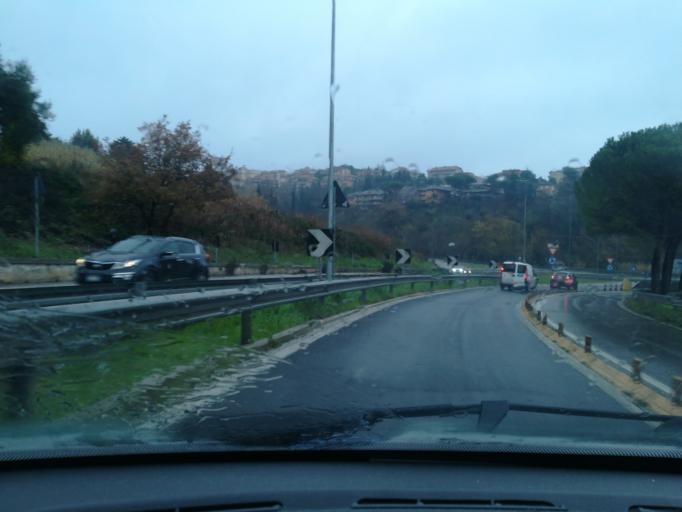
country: IT
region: The Marches
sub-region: Provincia di Macerata
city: Macerata
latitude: 43.2908
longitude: 13.4417
